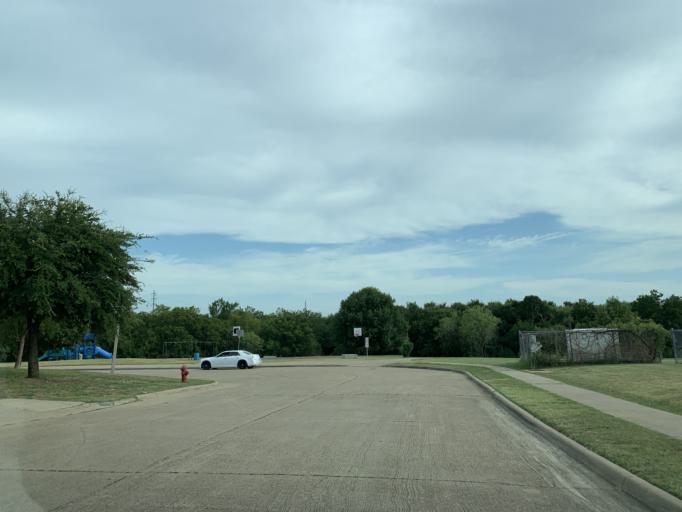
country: US
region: Texas
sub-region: Dallas County
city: Grand Prairie
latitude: 32.6604
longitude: -97.0454
